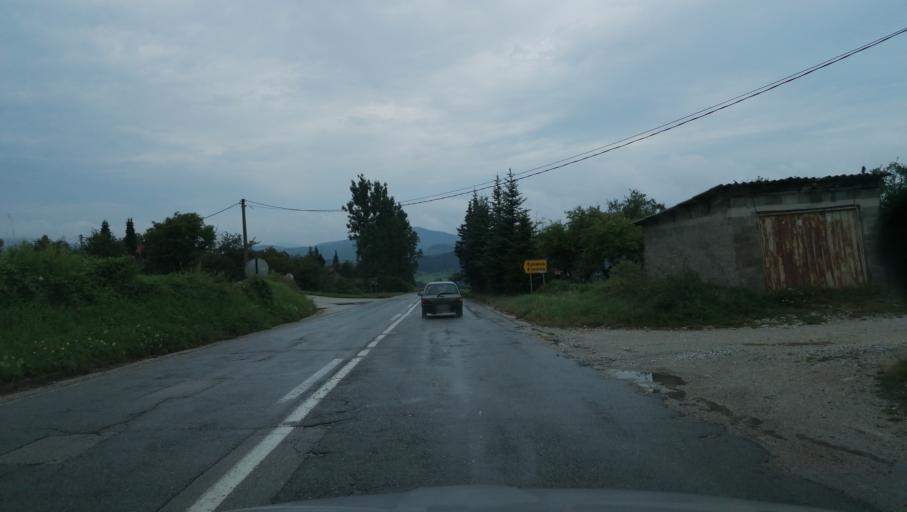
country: RS
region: Central Serbia
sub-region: Zlatiborski Okrug
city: Bajina Basta
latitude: 43.8449
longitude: 19.5940
